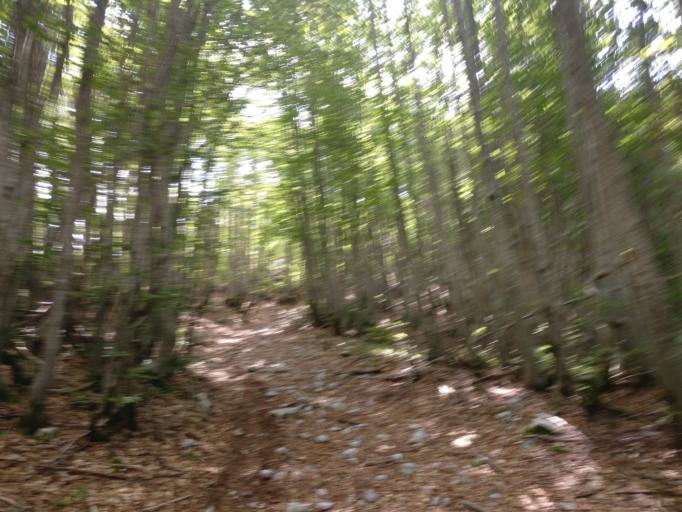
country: ME
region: Kotor
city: Kotor
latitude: 42.4079
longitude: 18.8400
